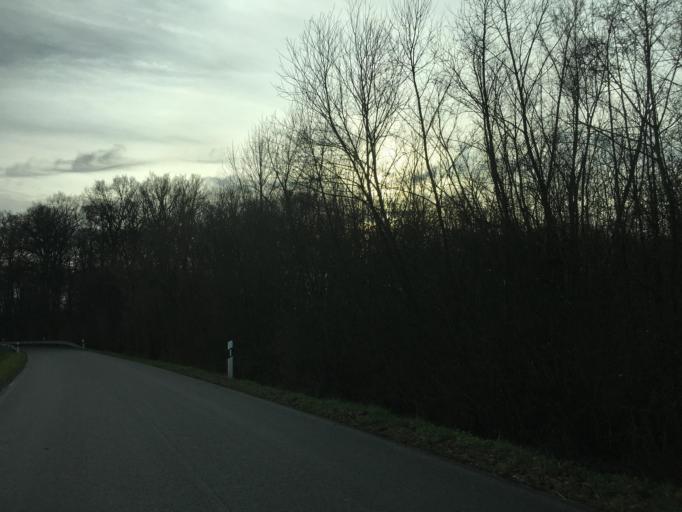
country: DE
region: North Rhine-Westphalia
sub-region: Regierungsbezirk Munster
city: Dulmen
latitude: 51.8279
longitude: 7.3558
